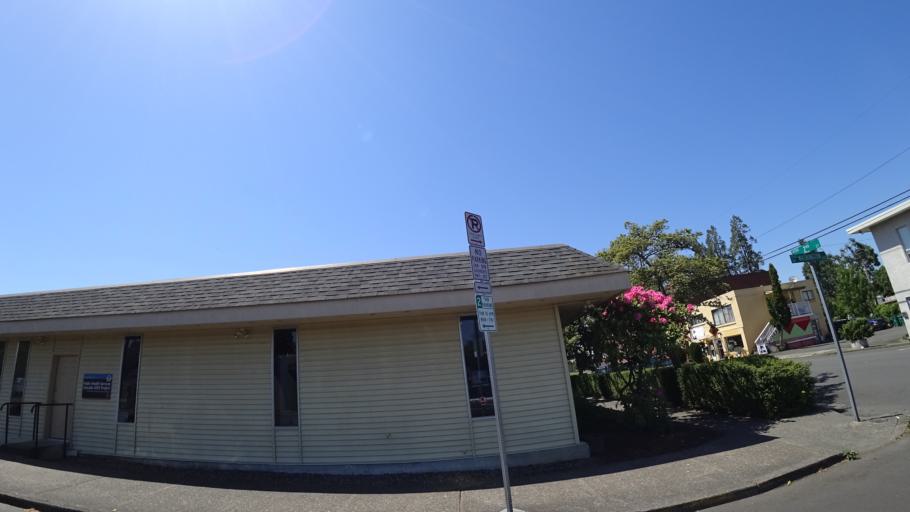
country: US
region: Oregon
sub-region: Washington County
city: Beaverton
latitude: 45.4855
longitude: -122.8054
